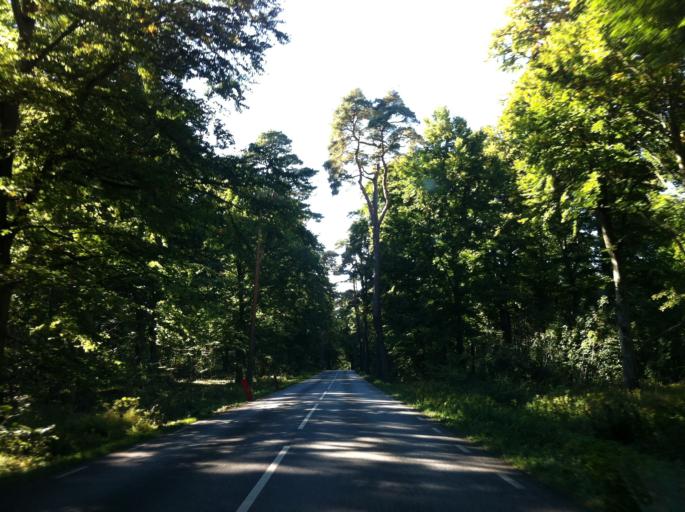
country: SE
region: Skane
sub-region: Sjobo Kommun
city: Sjoebo
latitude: 55.6920
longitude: 13.6241
